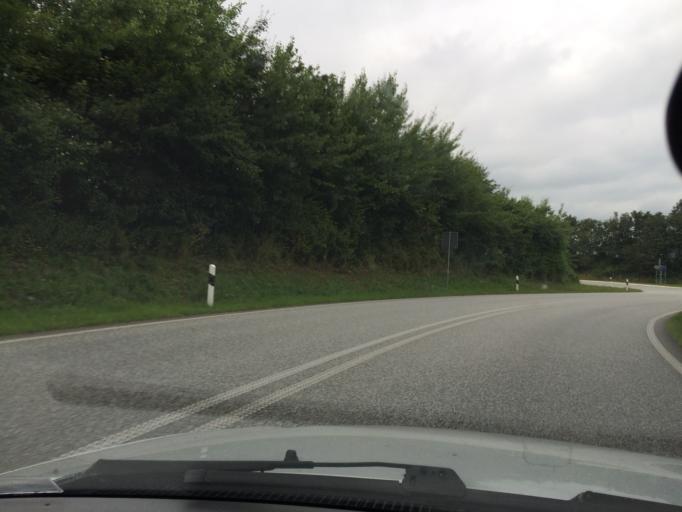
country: DE
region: Schleswig-Holstein
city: Tarp
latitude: 54.6631
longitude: 9.4275
